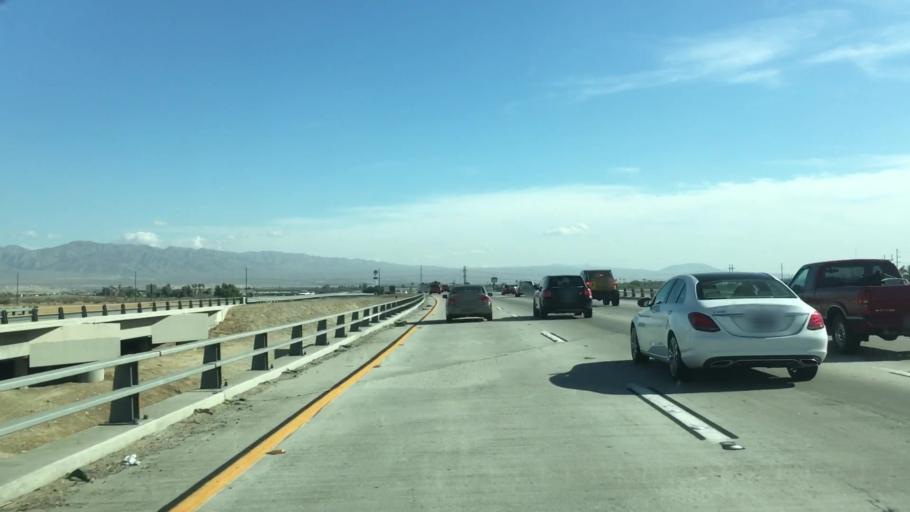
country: US
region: California
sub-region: Riverside County
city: Indio
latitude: 33.7387
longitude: -116.2487
